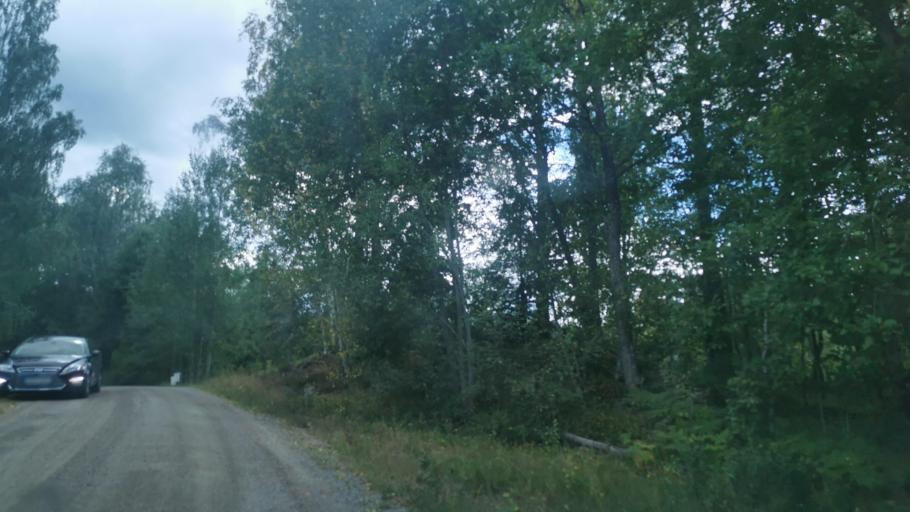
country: SE
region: OEstergoetland
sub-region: Finspangs Kommun
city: Finspang
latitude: 58.7907
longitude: 15.7685
